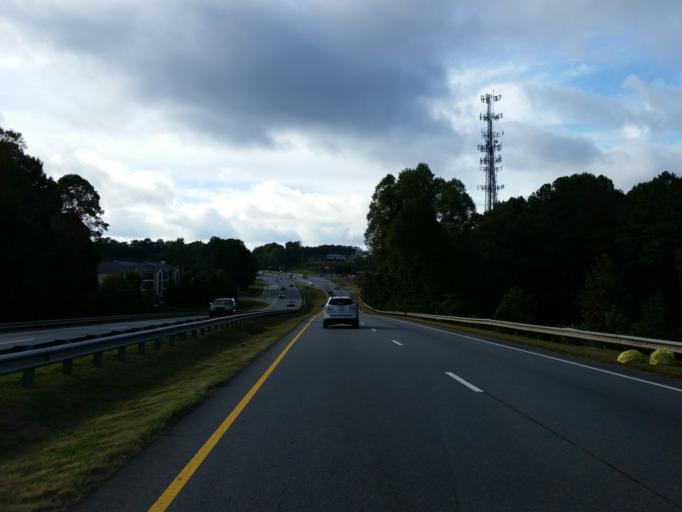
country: US
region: Georgia
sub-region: Cobb County
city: Kennesaw
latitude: 34.0254
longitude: -84.6331
